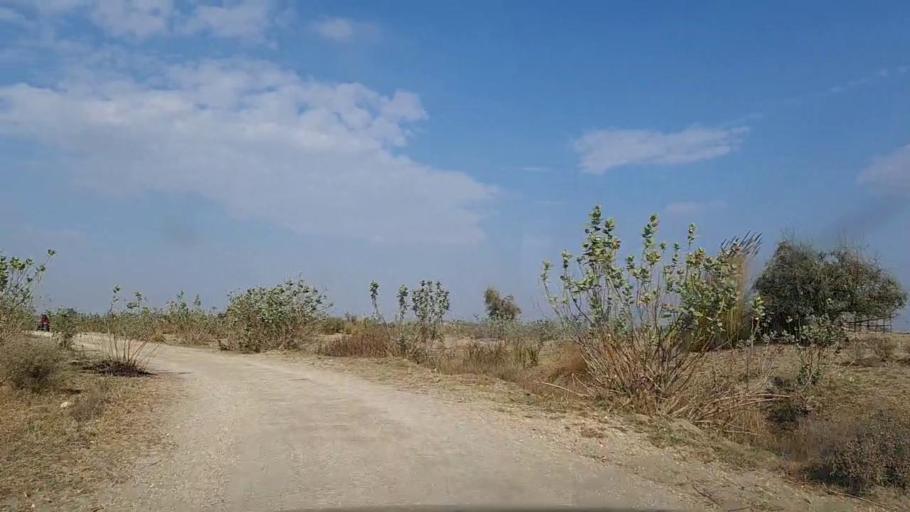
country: PK
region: Sindh
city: Sanghar
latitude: 26.2658
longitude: 69.0118
